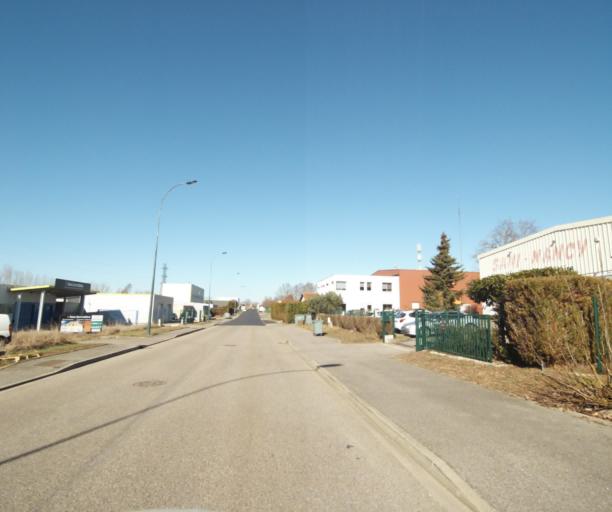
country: FR
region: Lorraine
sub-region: Departement de Meurthe-et-Moselle
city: Heillecourt
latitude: 48.6492
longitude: 6.2097
